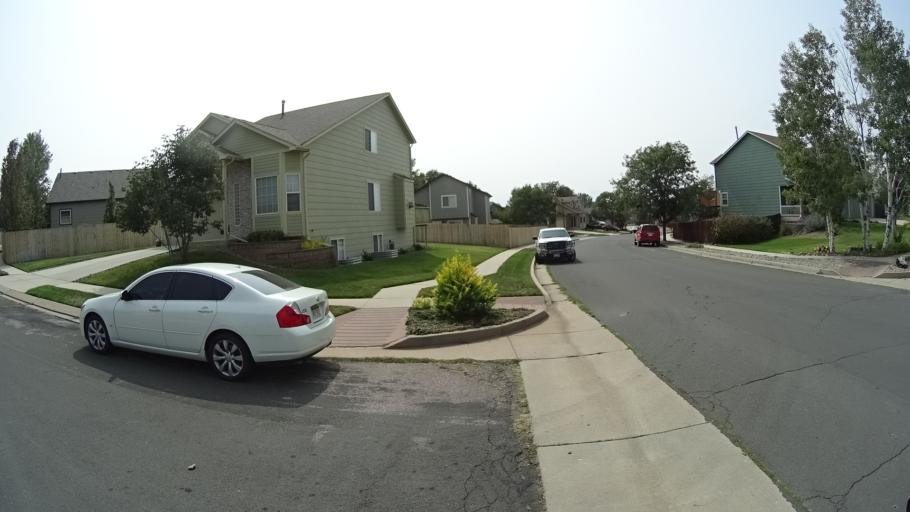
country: US
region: Colorado
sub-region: El Paso County
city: Cimarron Hills
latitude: 38.9233
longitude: -104.7262
